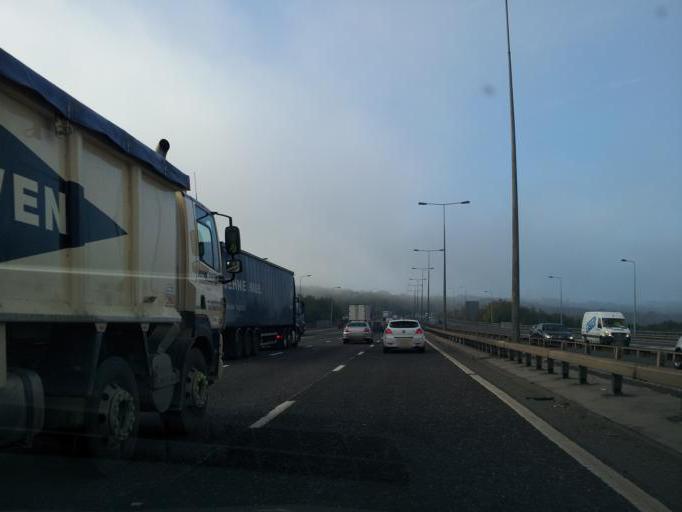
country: GB
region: England
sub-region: Calderdale
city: Brighouse
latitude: 53.6927
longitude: -1.7563
